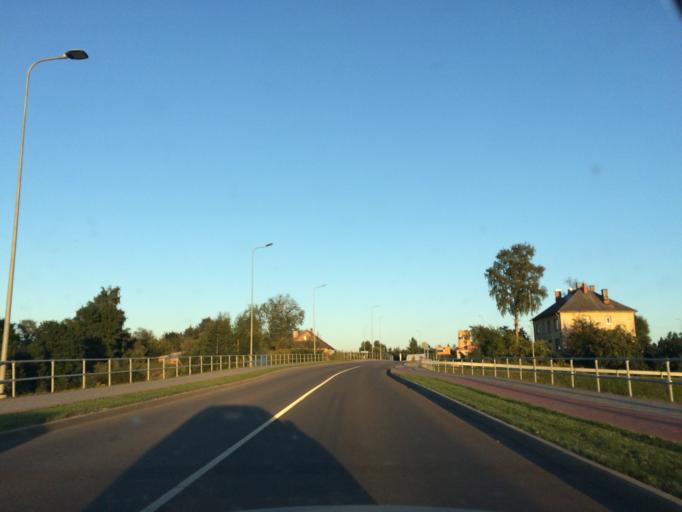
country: LV
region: Rezekne
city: Rezekne
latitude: 56.5137
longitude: 27.3561
